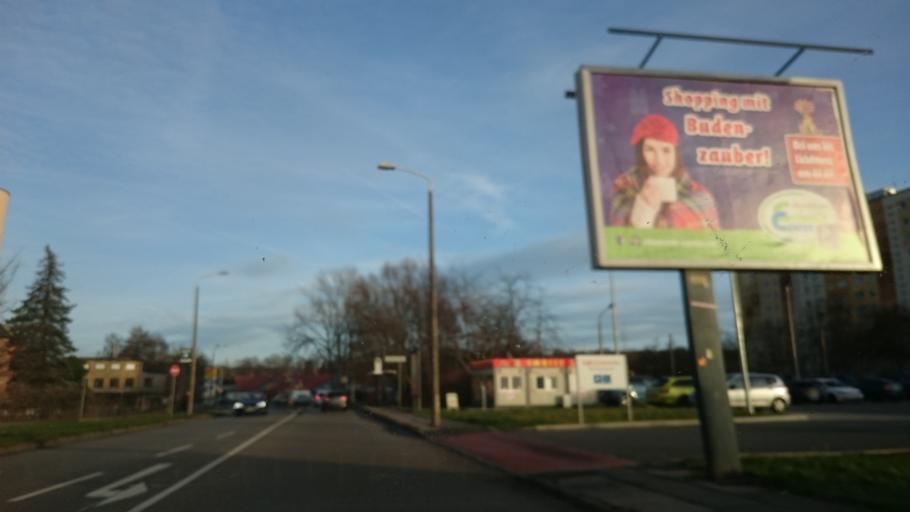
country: DE
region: Saxony
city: Zwickau
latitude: 50.7383
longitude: 12.4914
